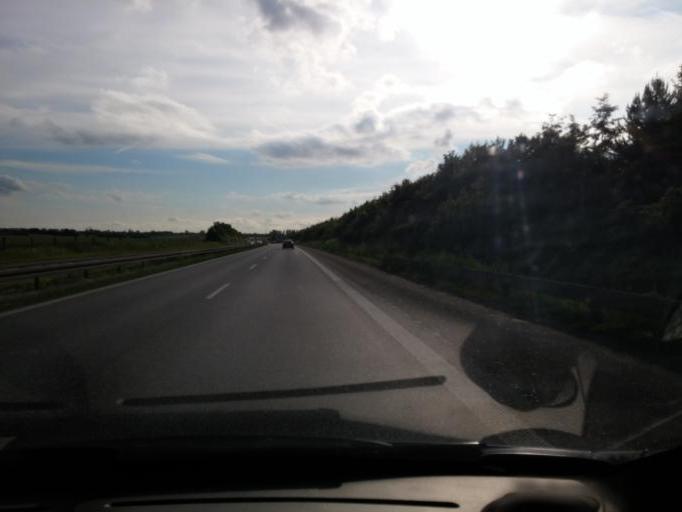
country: DK
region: Zealand
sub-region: Slagelse Kommune
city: Slagelse
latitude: 55.4321
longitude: 11.4521
